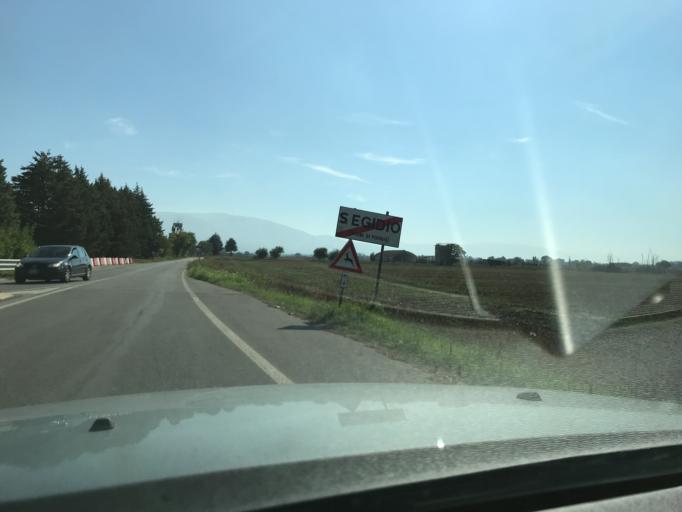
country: IT
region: Umbria
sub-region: Provincia di Perugia
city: Ospedalicchio
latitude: 43.0936
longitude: 12.4990
